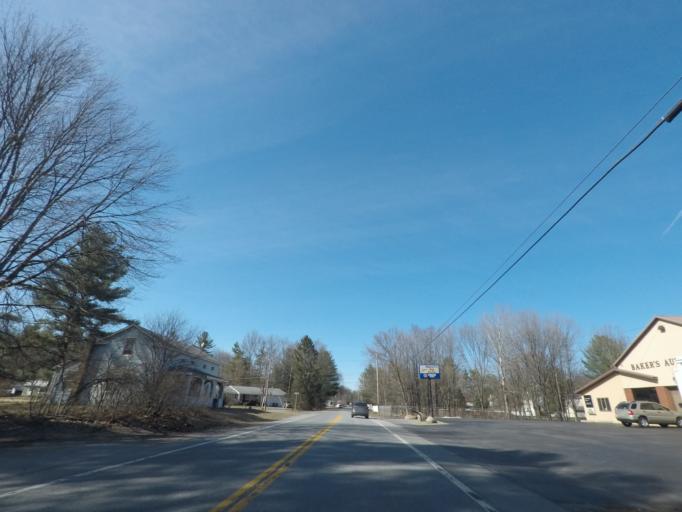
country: US
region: New York
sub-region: Saratoga County
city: Milton
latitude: 43.0318
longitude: -73.8485
